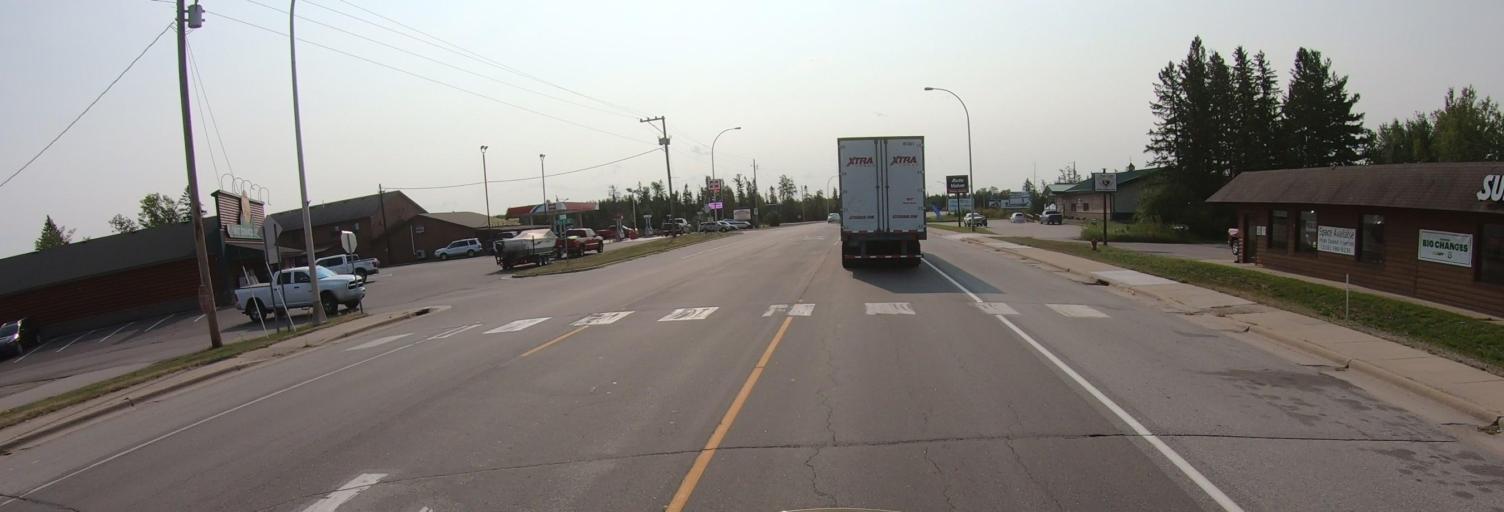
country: US
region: Minnesota
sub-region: Saint Louis County
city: Mountain Iron
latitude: 47.8484
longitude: -92.6850
